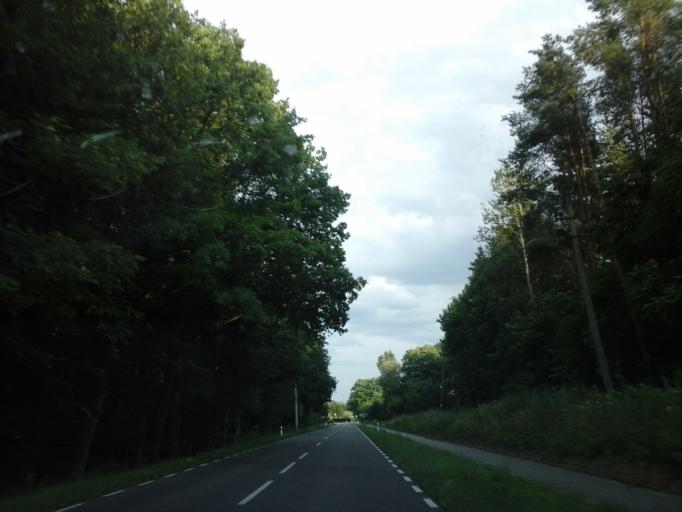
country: PL
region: West Pomeranian Voivodeship
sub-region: Powiat kamienski
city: Golczewo
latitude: 53.8654
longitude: 14.9059
